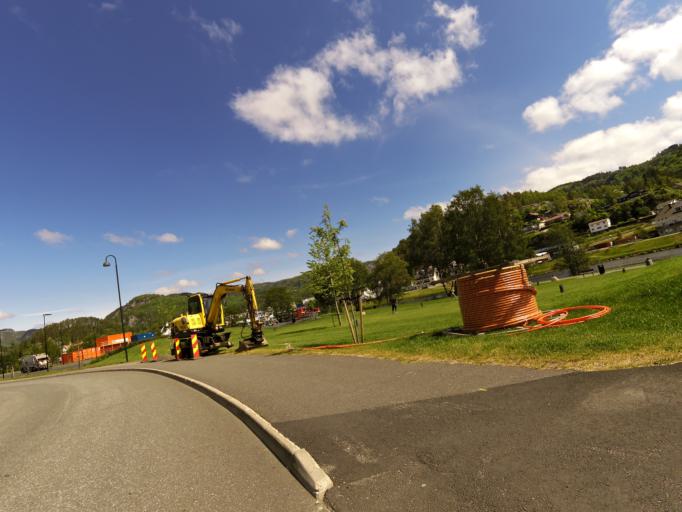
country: NO
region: Vest-Agder
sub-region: Kvinesdal
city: Liknes
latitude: 58.3139
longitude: 6.9595
